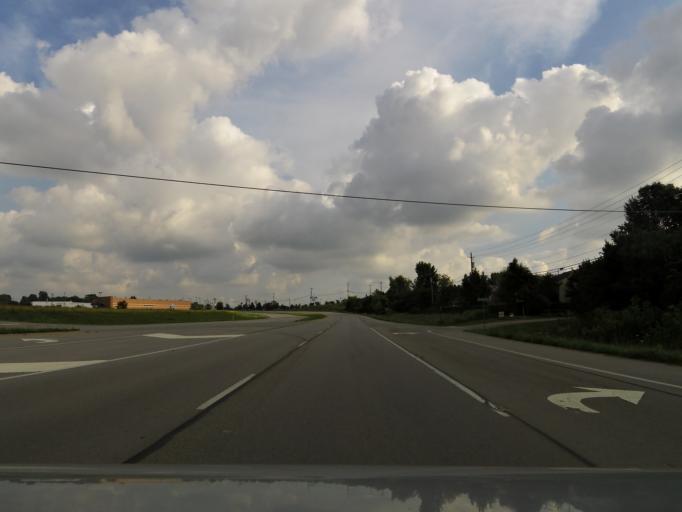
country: US
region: Kentucky
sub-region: Bourbon County
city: Paris
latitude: 38.2015
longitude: -84.2756
